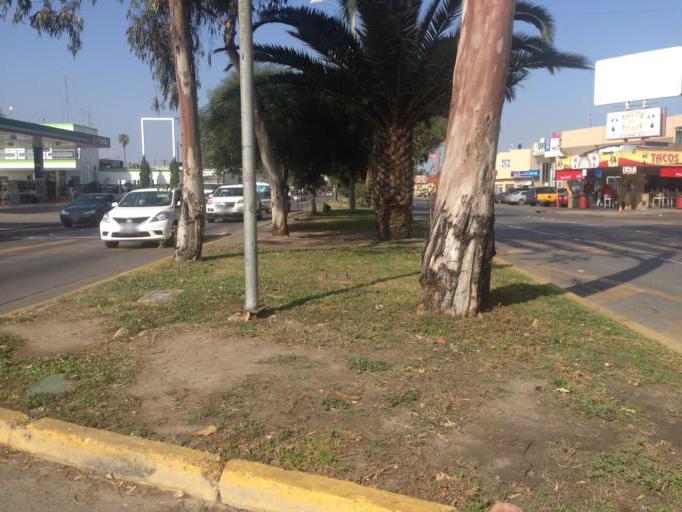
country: MX
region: Baja California
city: Tijuana
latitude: 32.5278
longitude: -117.0264
